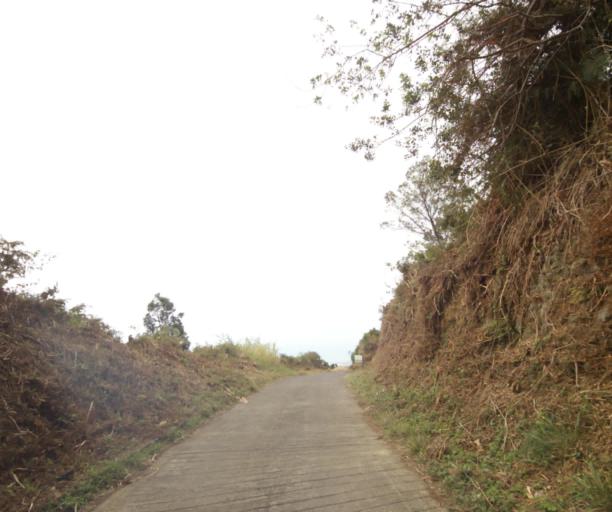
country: RE
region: Reunion
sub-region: Reunion
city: Saint-Paul
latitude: -21.0211
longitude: 55.3251
